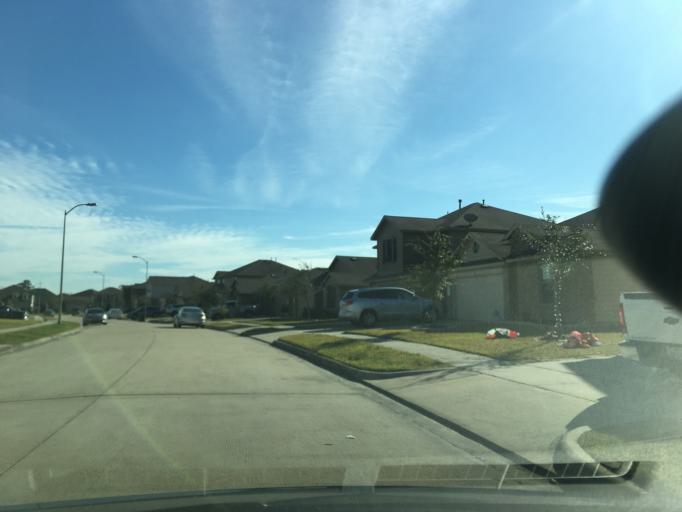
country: US
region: Texas
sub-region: Harris County
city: Cloverleaf
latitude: 29.8145
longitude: -95.1604
